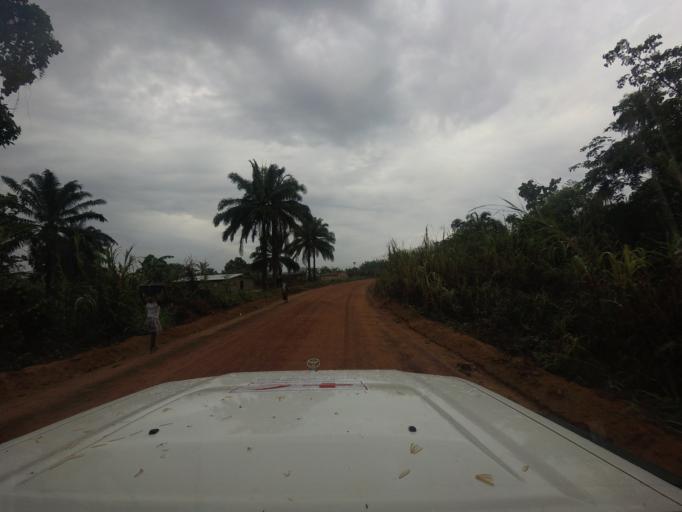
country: LR
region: Lofa
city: Voinjama
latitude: 8.3982
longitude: -9.7863
